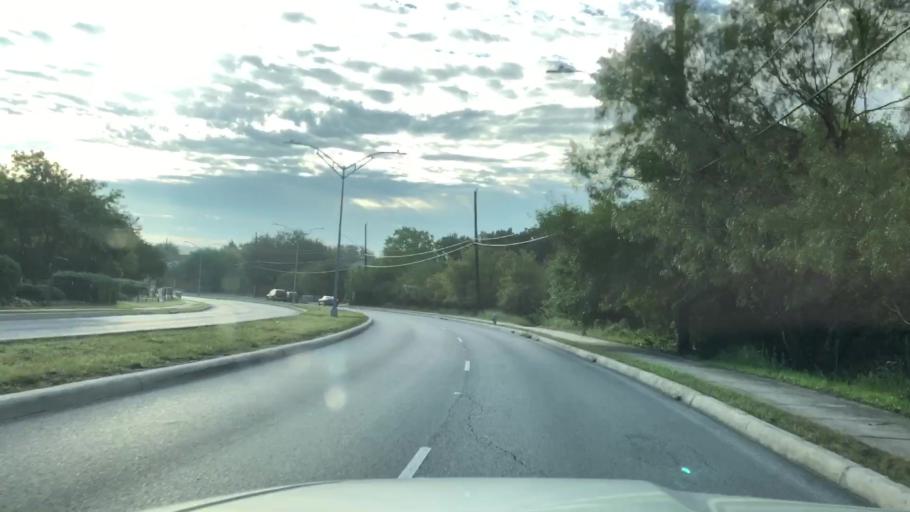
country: US
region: Texas
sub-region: Bexar County
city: Leon Valley
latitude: 29.5421
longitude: -98.6366
